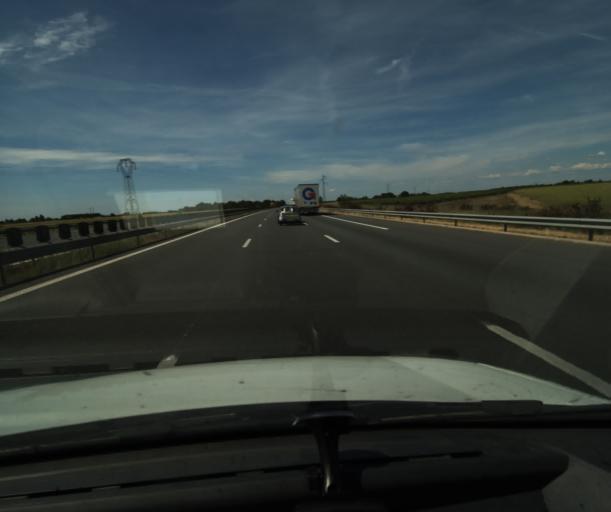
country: FR
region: Midi-Pyrenees
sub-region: Departement du Tarn-et-Garonne
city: Grisolles
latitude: 43.8514
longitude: 1.3195
